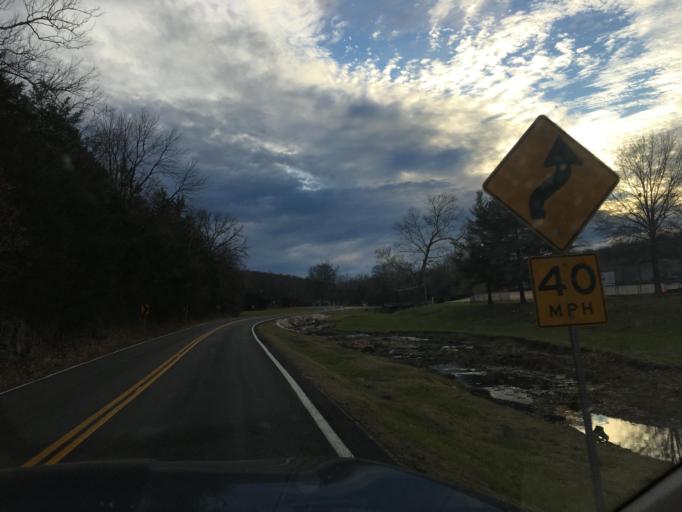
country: US
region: Missouri
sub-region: Jefferson County
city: De Soto
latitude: 38.1121
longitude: -90.5621
